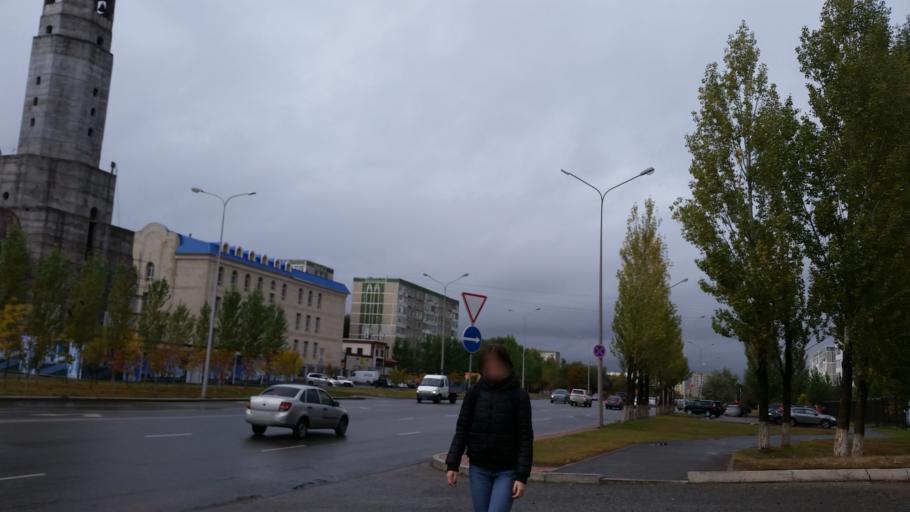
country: KZ
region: Astana Qalasy
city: Astana
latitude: 51.1497
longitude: 71.4828
